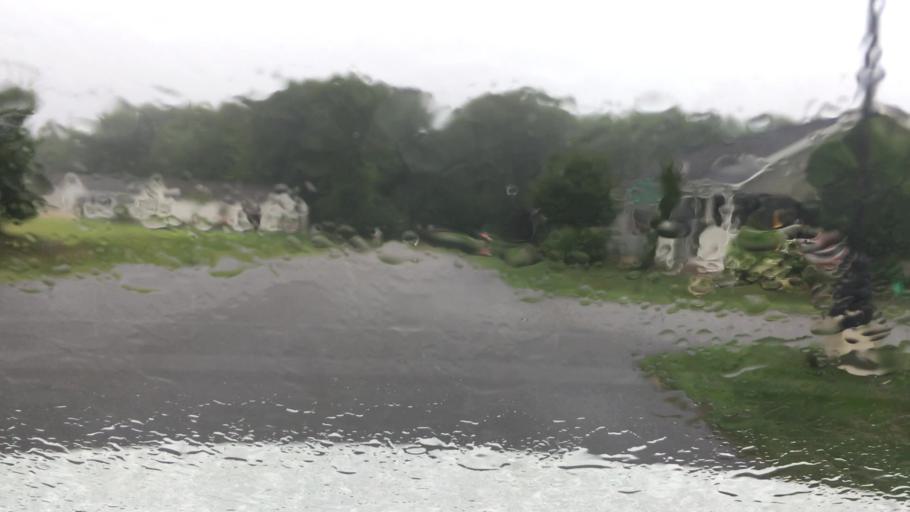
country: US
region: Maine
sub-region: Cumberland County
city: Scarborough
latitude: 43.5982
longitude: -70.3130
